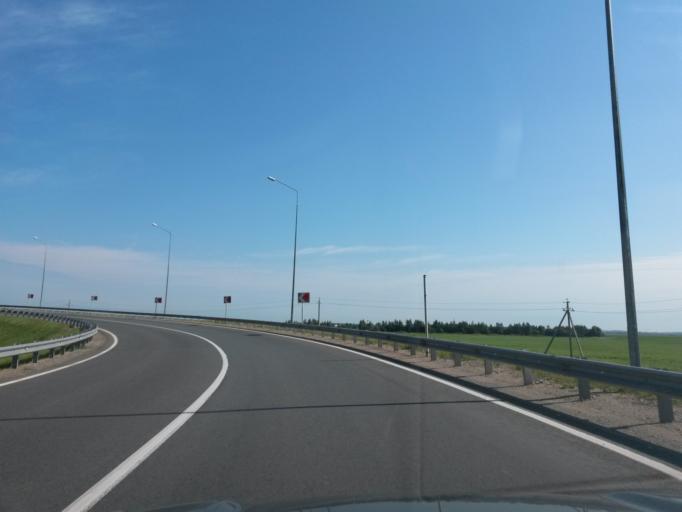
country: RU
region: Jaroslavl
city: Yaroslavl
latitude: 57.7372
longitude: 39.8995
